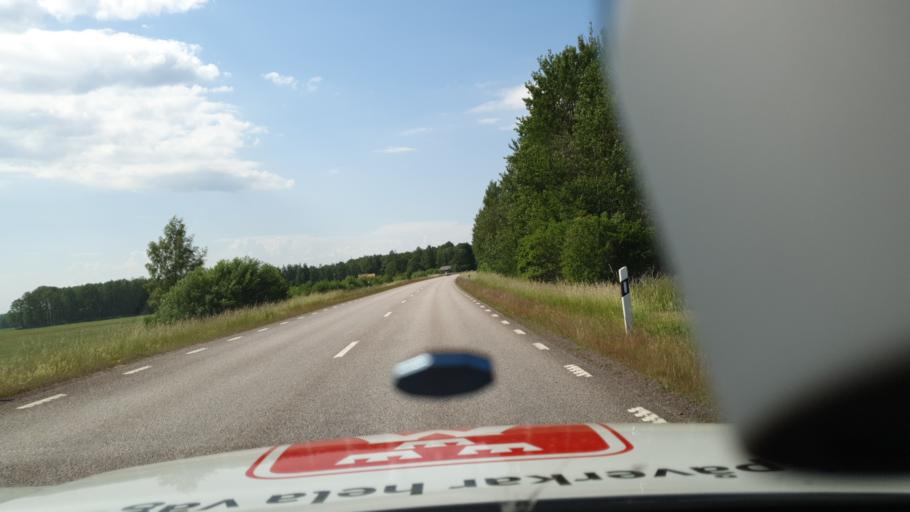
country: SE
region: Vaestra Goetaland
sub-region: Hjo Kommun
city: Hjo
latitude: 58.2415
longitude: 14.2281
